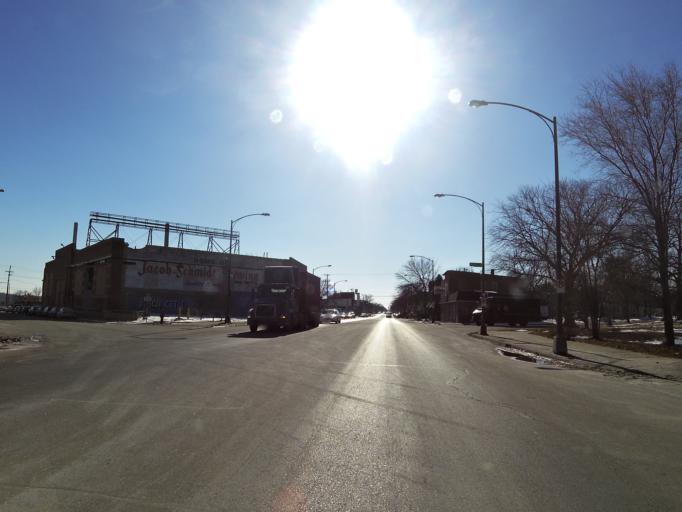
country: US
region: Minnesota
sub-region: Dakota County
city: West Saint Paul
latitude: 44.9294
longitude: -93.1244
